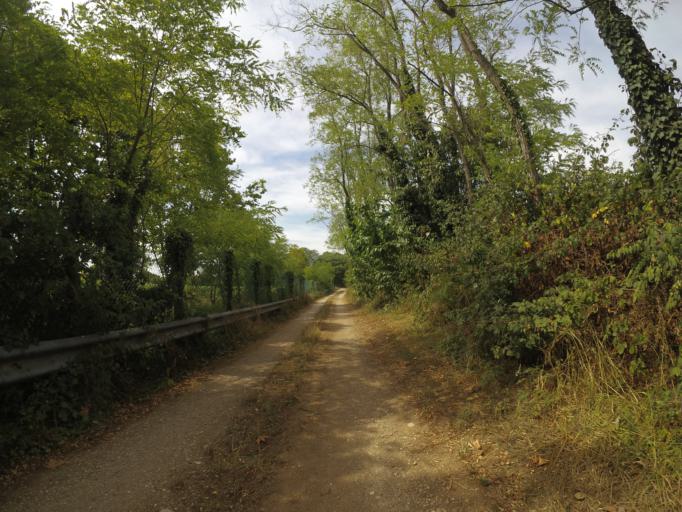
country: IT
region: Friuli Venezia Giulia
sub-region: Provincia di Udine
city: Talmassons
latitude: 45.9580
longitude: 13.1044
